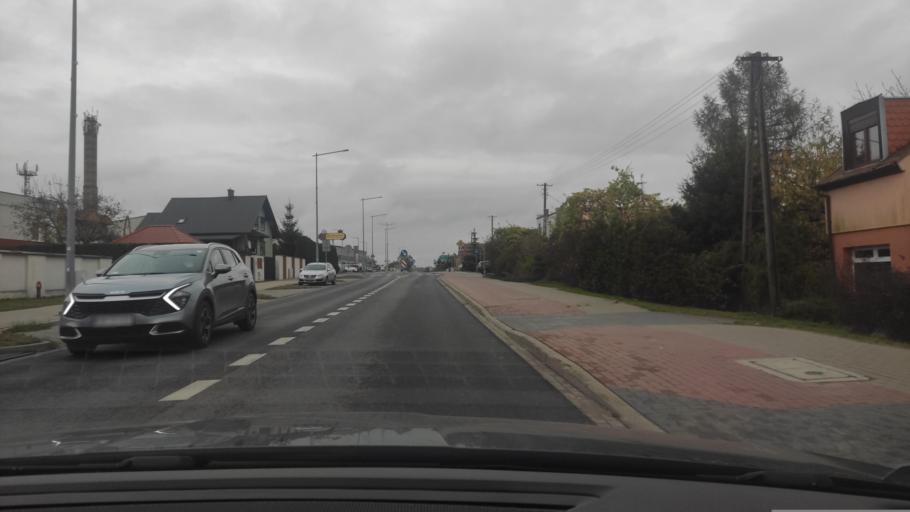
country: PL
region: Greater Poland Voivodeship
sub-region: Powiat poznanski
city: Kostrzyn
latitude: 52.3980
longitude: 17.2329
